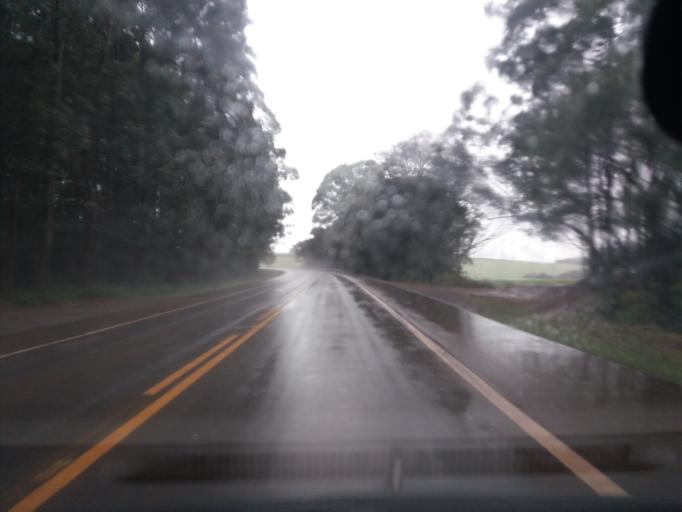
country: BR
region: Parana
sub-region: Campo Mourao
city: Campo Mourao
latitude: -24.2874
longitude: -52.5640
